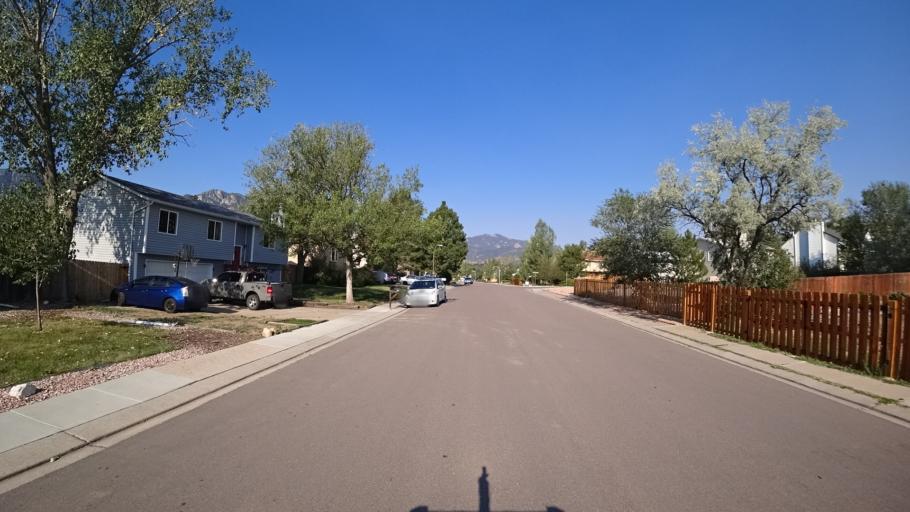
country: US
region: Colorado
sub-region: El Paso County
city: Stratmoor
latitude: 38.7795
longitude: -104.8120
